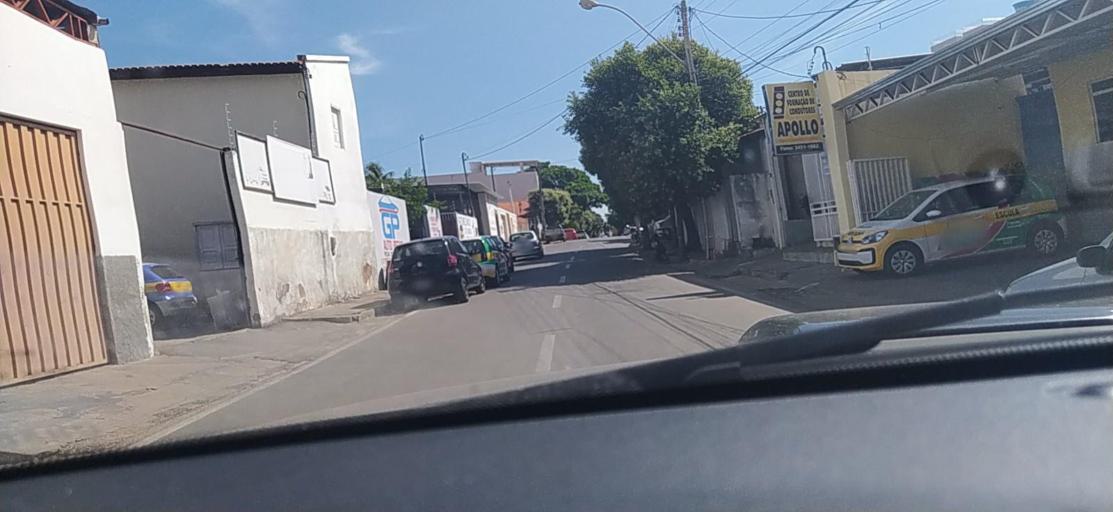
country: BR
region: Bahia
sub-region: Guanambi
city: Guanambi
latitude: -14.2214
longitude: -42.7754
